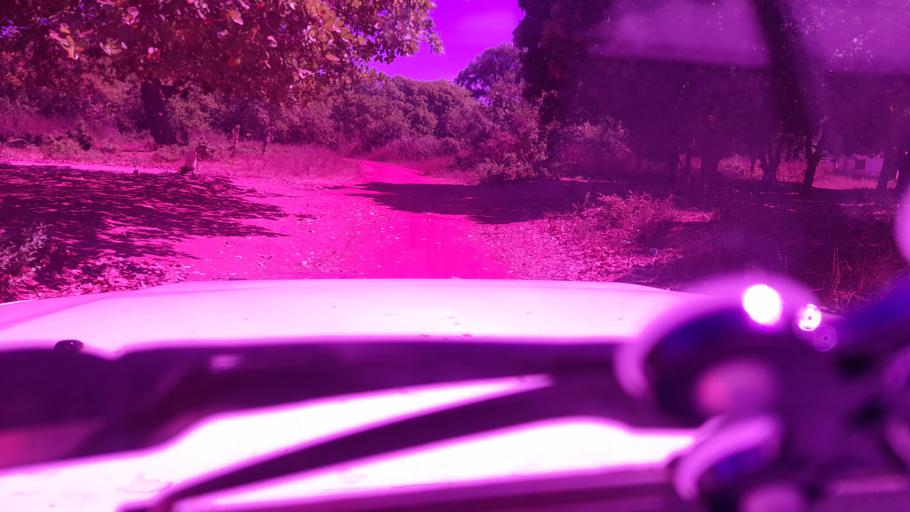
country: GW
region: Oio
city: Bissora
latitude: 12.3903
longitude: -15.6212
